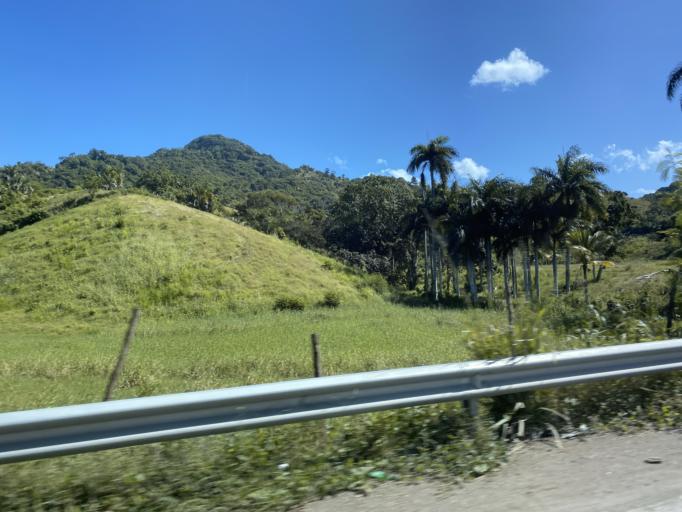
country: DO
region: Puerto Plata
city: Imbert
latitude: 19.8151
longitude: -70.7794
